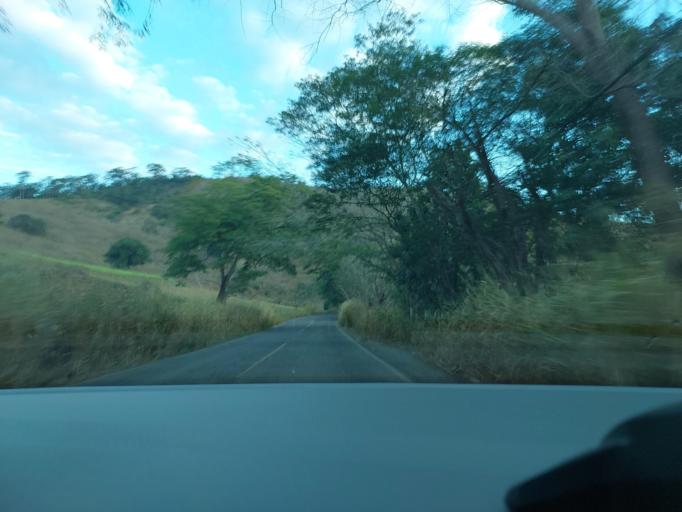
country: BR
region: Rio de Janeiro
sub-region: Natividade
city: Natividade
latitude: -21.1976
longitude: -42.1170
